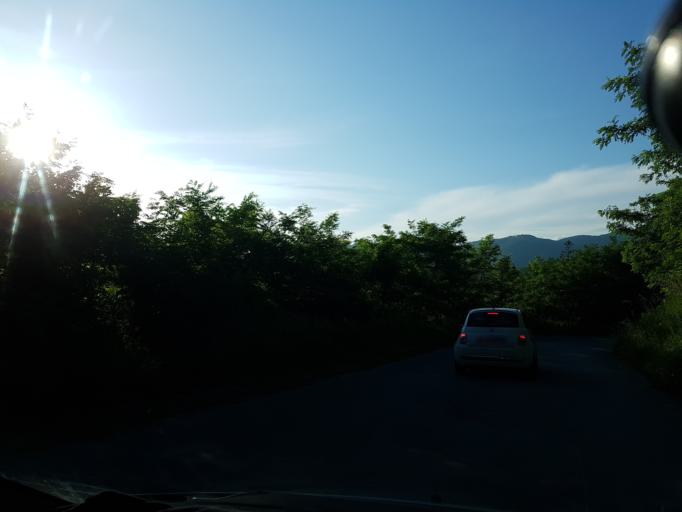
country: IT
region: Tuscany
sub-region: Provincia di Massa-Carrara
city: Casola in Lunigiana
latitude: 44.1879
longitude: 10.1928
